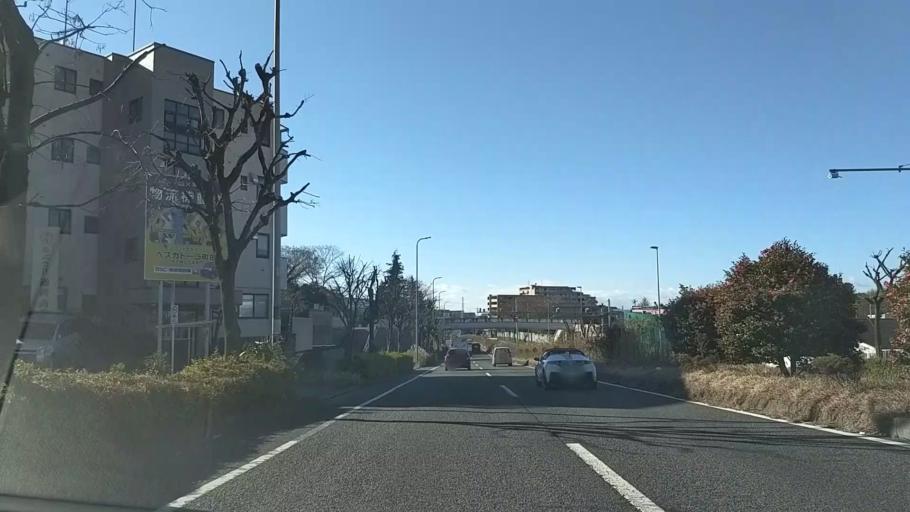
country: JP
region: Kanagawa
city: Minami-rinkan
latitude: 35.5050
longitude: 139.4718
